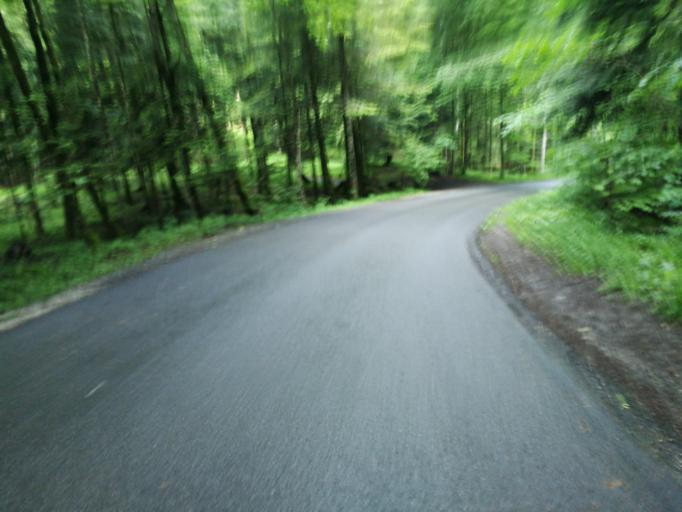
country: CH
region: Schwyz
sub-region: Bezirk Hoefe
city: Feusisberg
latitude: 47.1753
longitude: 8.7733
